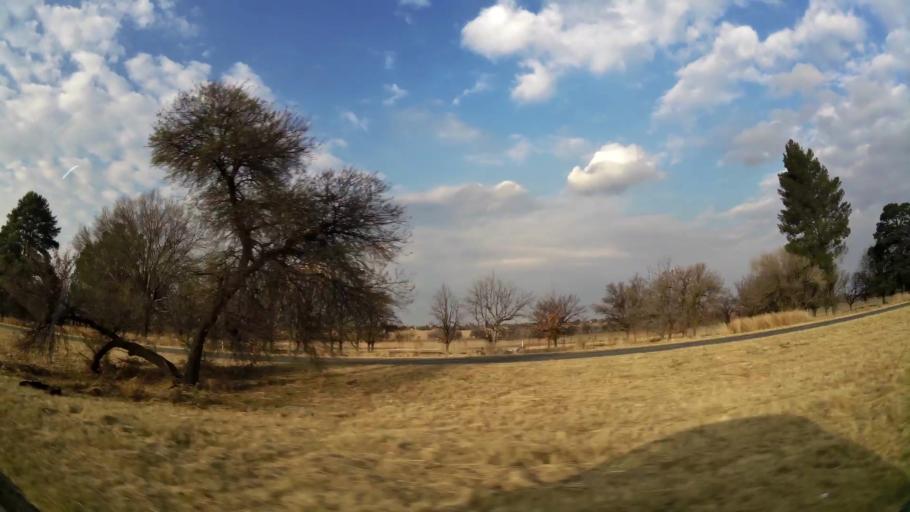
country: ZA
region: Orange Free State
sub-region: Fezile Dabi District Municipality
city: Sasolburg
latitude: -26.7744
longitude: 27.8247
